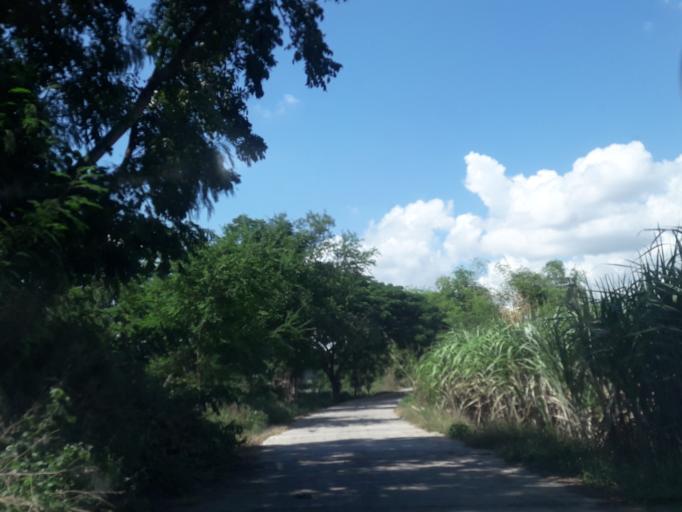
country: TH
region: Lop Buri
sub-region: Amphoe Tha Luang
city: Tha Luang
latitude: 15.0682
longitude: 101.0426
